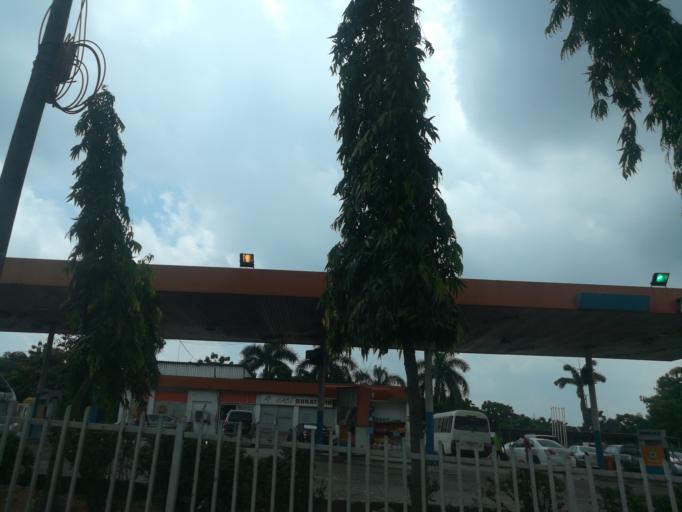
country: NG
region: Lagos
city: Ojota
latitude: 6.5973
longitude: 3.3680
